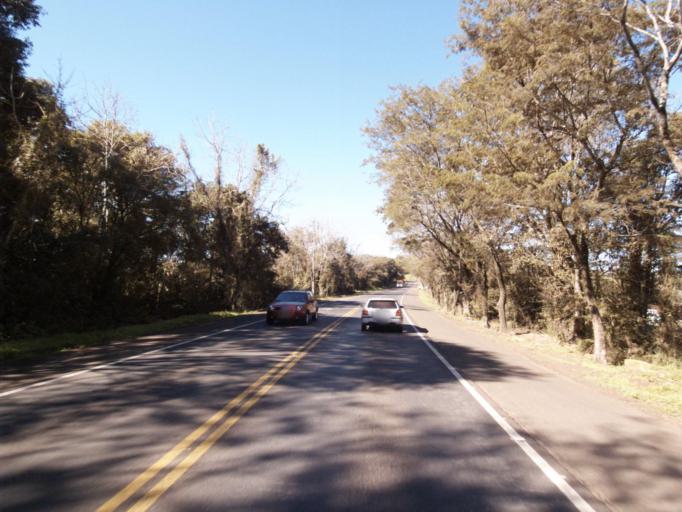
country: BR
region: Santa Catarina
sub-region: Chapeco
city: Chapeco
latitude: -26.8989
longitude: -52.8738
